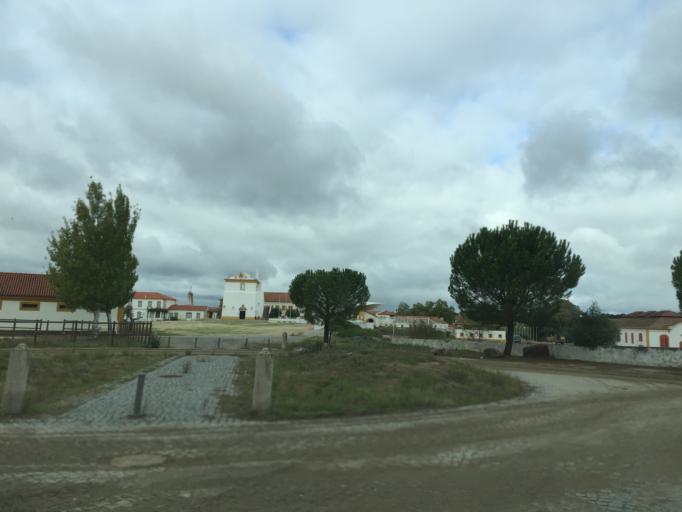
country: PT
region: Portalegre
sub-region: Alter do Chao
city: Alter do Chao
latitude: 39.2212
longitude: -7.6849
